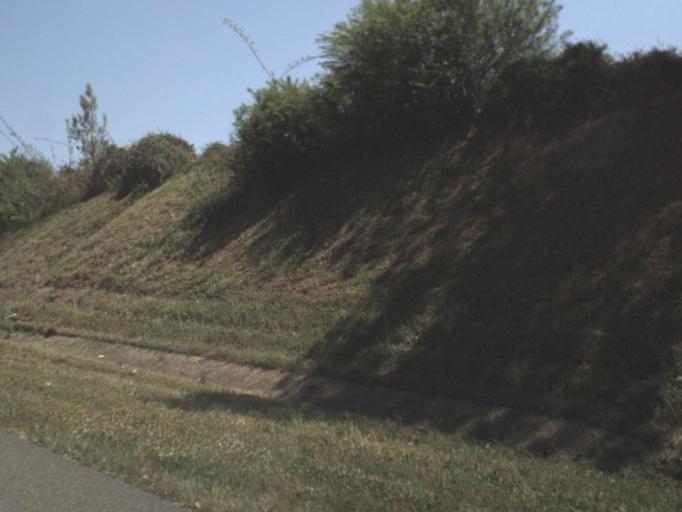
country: US
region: Florida
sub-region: Escambia County
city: Century
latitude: 30.9486
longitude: -87.1837
